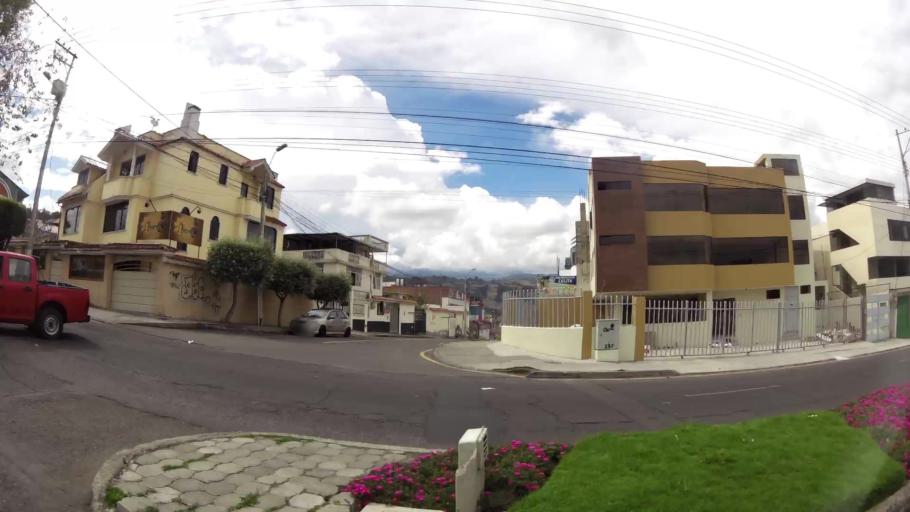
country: EC
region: Tungurahua
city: Ambato
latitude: -1.2690
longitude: -78.6352
